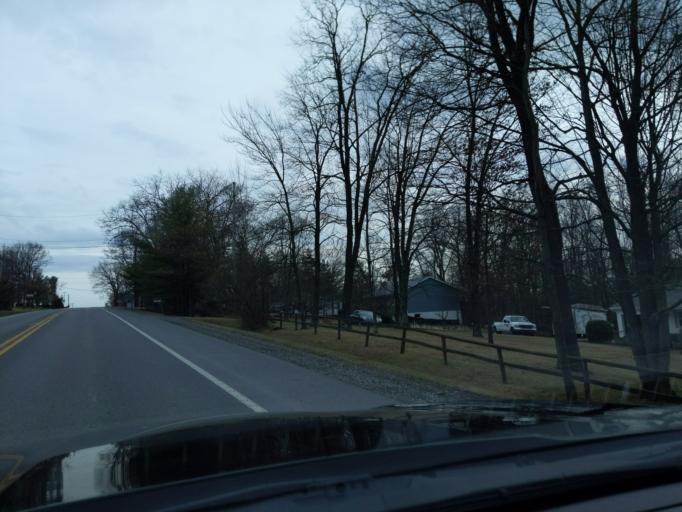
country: US
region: Pennsylvania
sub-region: Blair County
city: Lakemont
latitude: 40.4640
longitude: -78.3813
